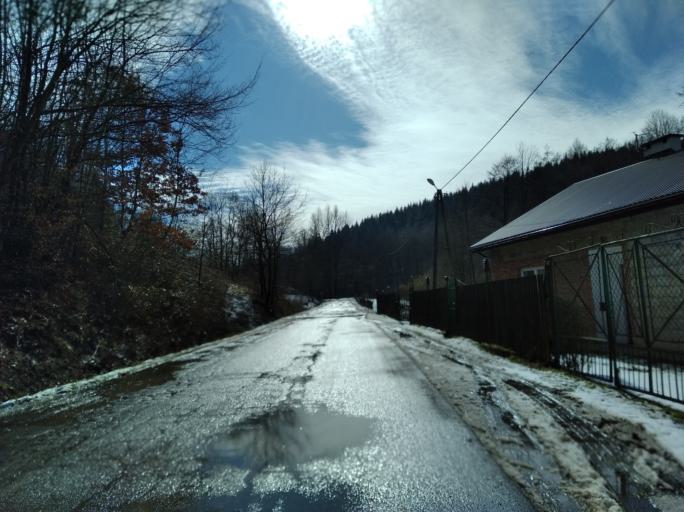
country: PL
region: Subcarpathian Voivodeship
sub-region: Powiat brzozowski
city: Jablonica Polska
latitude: 49.7392
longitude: 21.8865
